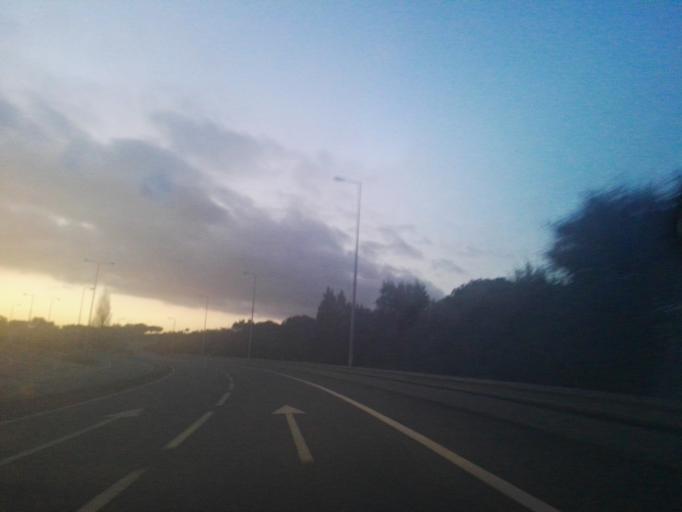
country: PT
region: Evora
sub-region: Montemor-O-Novo
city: Montemor-o-Novo
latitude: 38.6662
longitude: -8.1698
